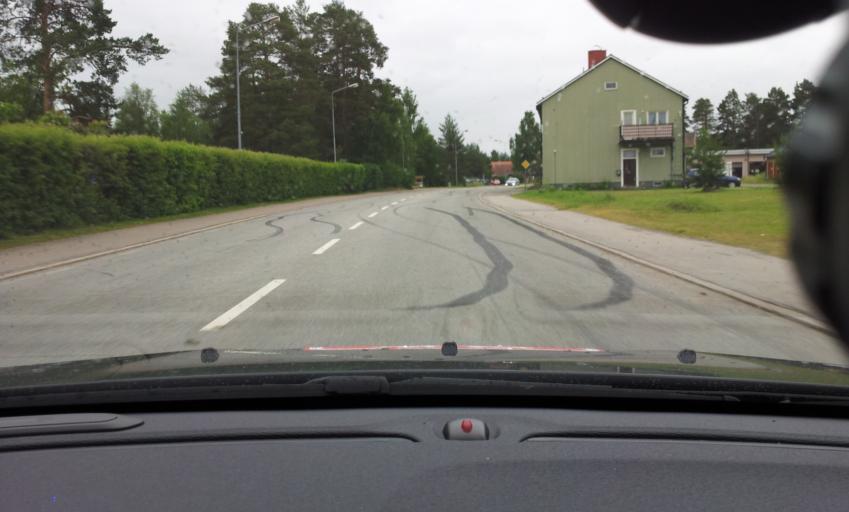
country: SE
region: Jaemtland
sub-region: Ragunda Kommun
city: Hammarstrand
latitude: 63.1062
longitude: 16.3572
